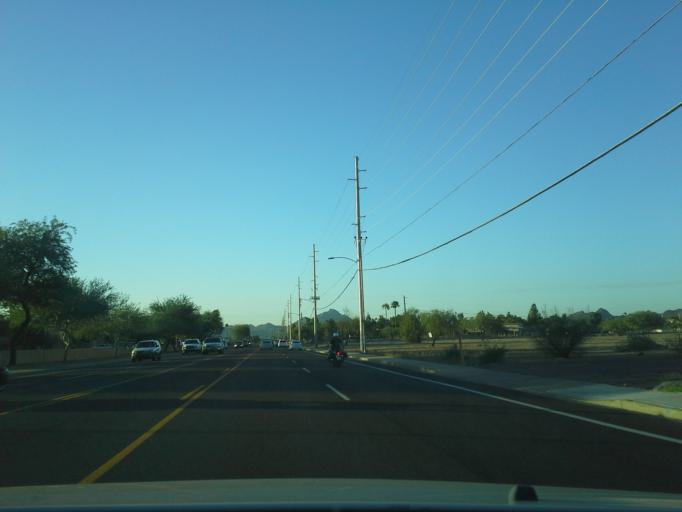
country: US
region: Arizona
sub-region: Maricopa County
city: Paradise Valley
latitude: 33.6174
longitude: -112.0134
